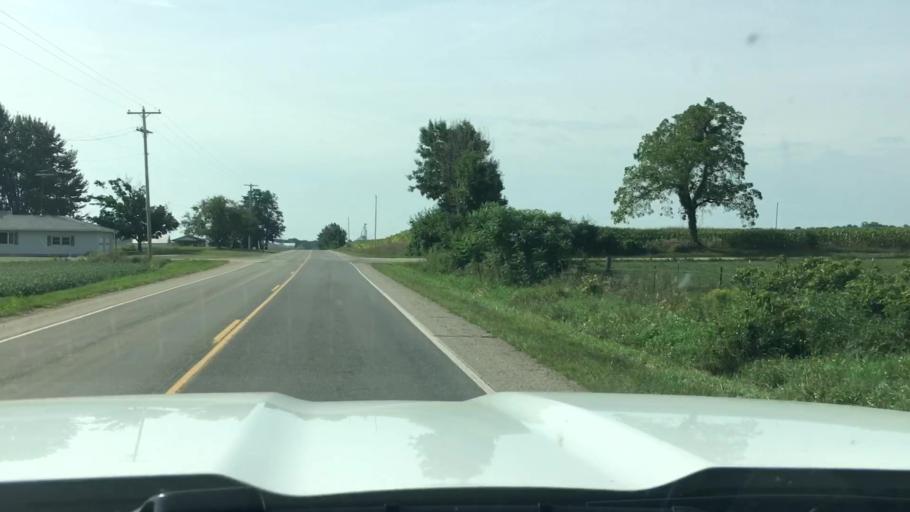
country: US
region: Michigan
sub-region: Allegan County
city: Plainwell
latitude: 42.5238
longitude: -85.6221
